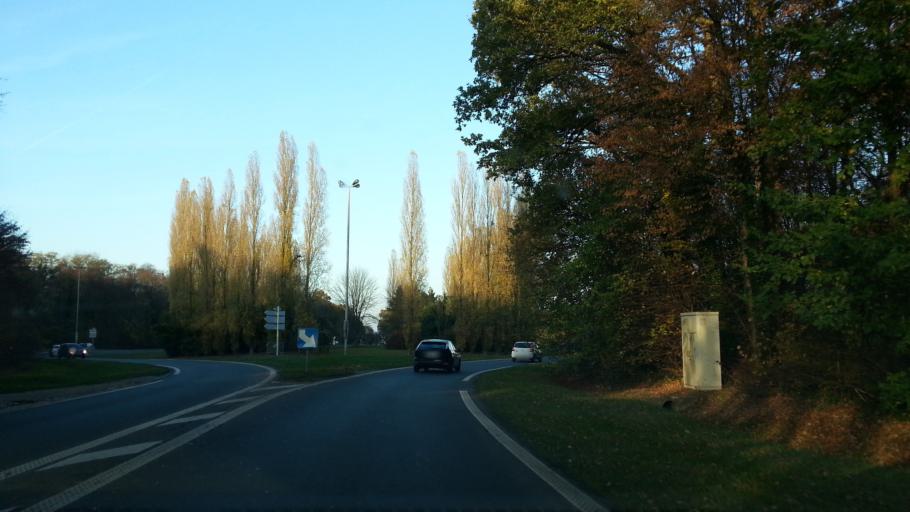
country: FR
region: Picardie
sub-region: Departement de l'Oise
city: Chantilly
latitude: 49.2047
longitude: 2.4618
